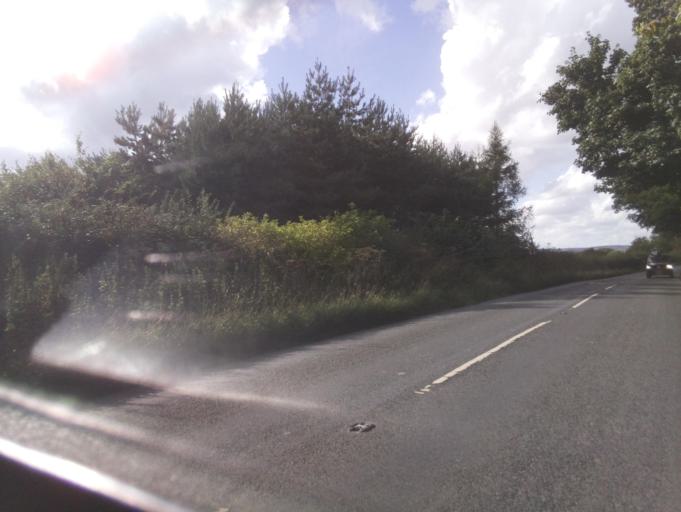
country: GB
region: England
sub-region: North Yorkshire
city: Bedale
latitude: 54.2099
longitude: -1.6164
